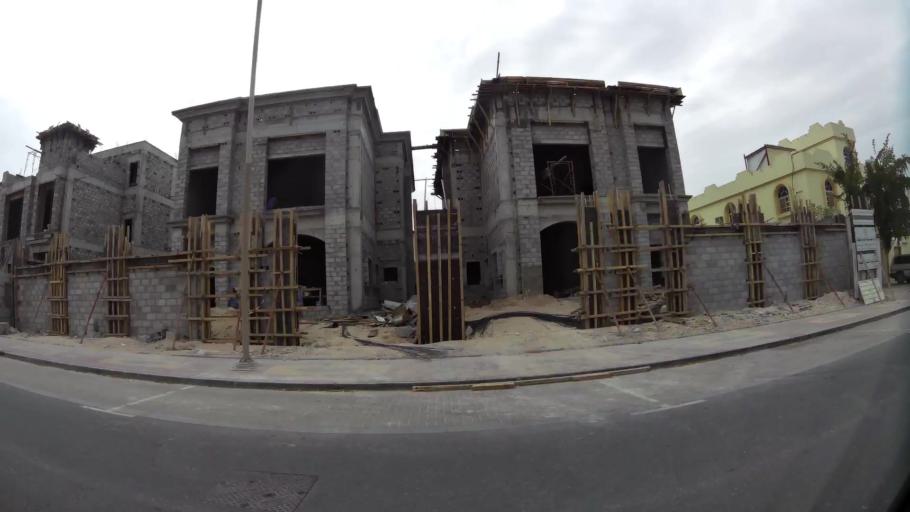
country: QA
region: Baladiyat ad Dawhah
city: Doha
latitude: 25.3404
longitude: 51.4877
